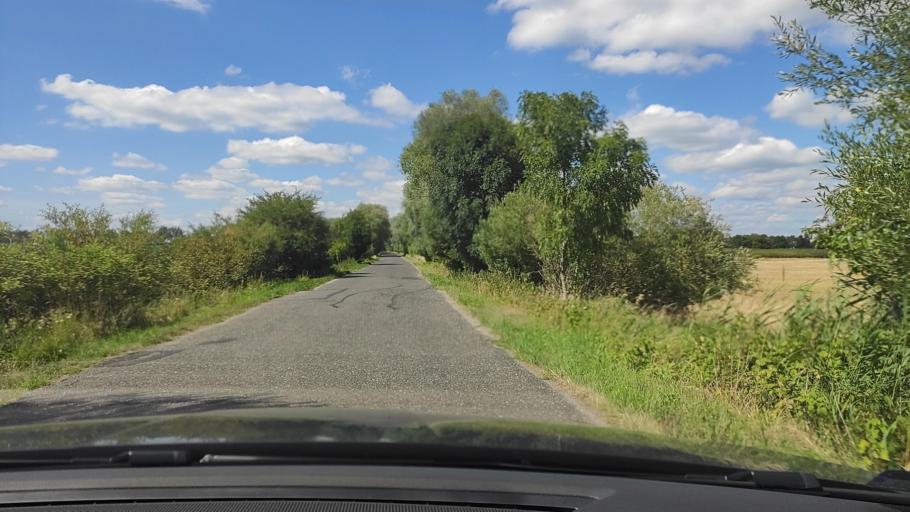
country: PL
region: Greater Poland Voivodeship
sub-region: Powiat poznanski
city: Kobylnica
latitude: 52.4922
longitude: 17.1313
